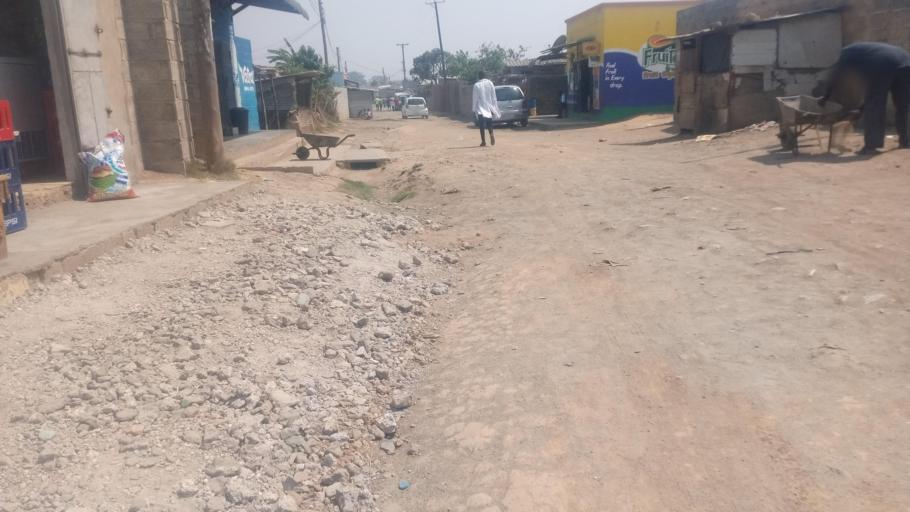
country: ZM
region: Lusaka
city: Lusaka
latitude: -15.4464
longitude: 28.3763
